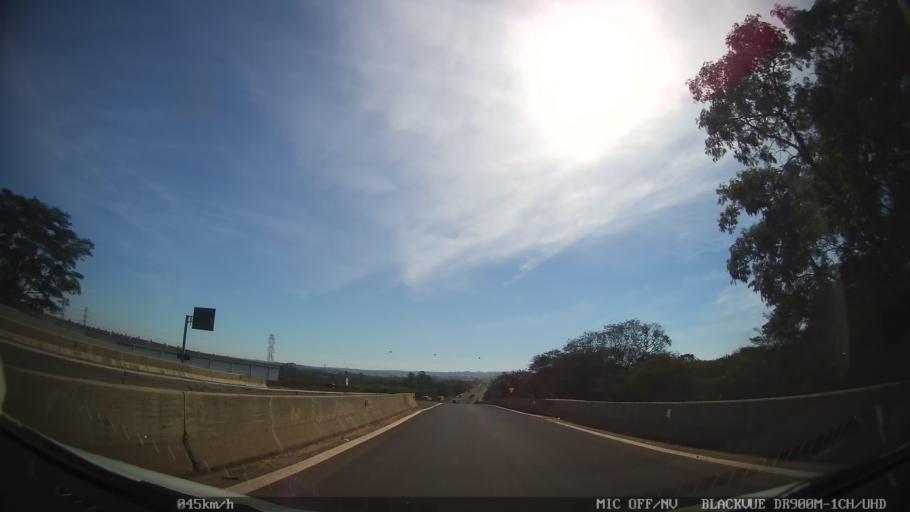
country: BR
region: Sao Paulo
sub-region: Porto Ferreira
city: Porto Ferreira
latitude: -21.8493
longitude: -47.4949
